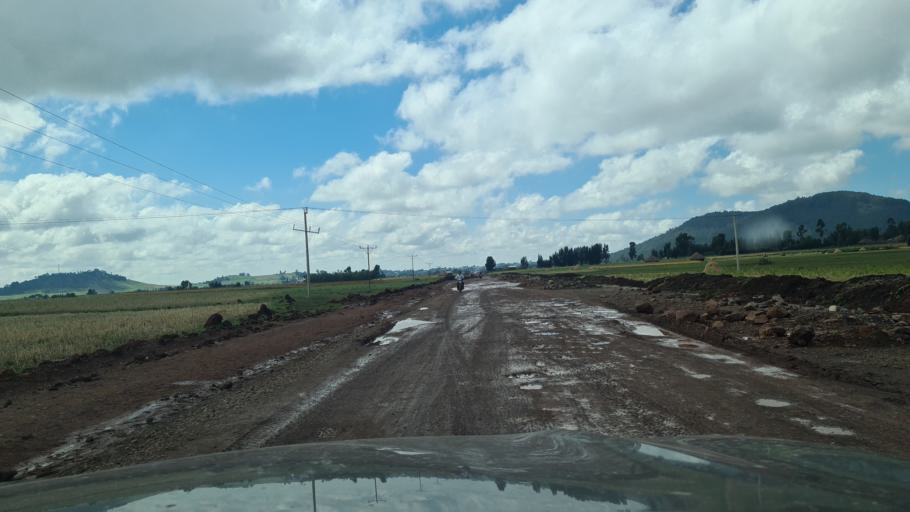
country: ET
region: Oromiya
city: Huruta
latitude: 8.0915
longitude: 39.5375
